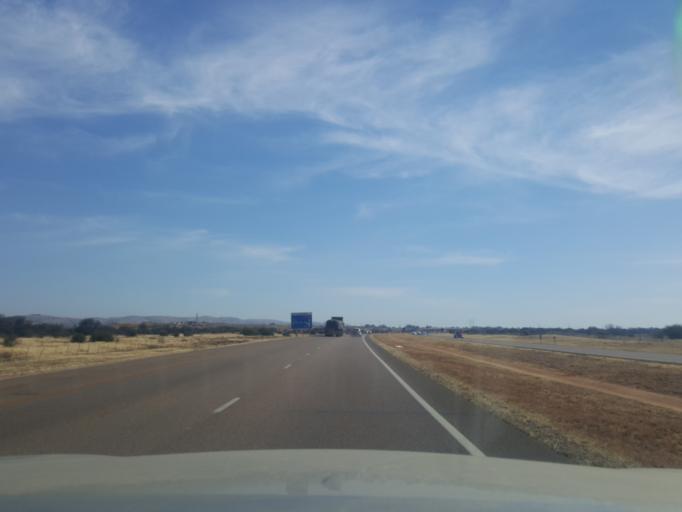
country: ZA
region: Gauteng
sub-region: City of Tshwane Metropolitan Municipality
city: Pretoria
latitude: -25.6453
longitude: 28.1670
